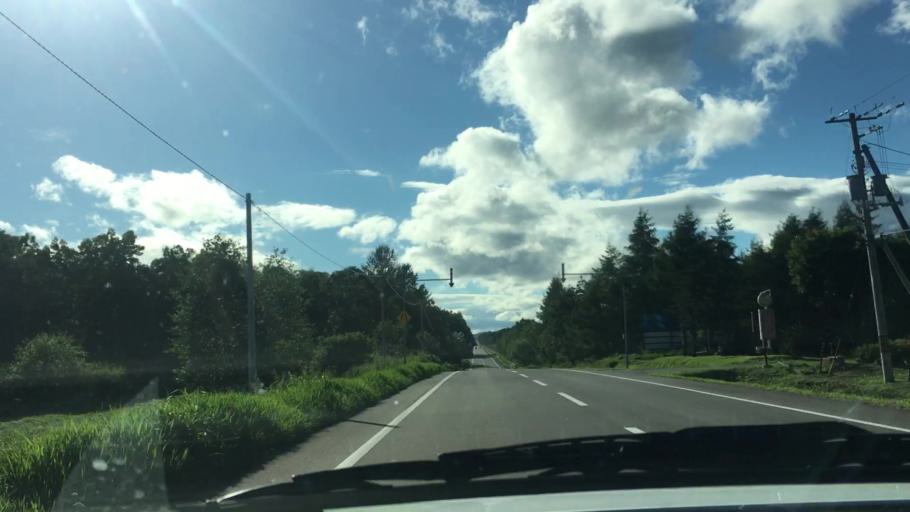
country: JP
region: Hokkaido
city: Otofuke
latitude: 43.1659
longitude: 143.1347
